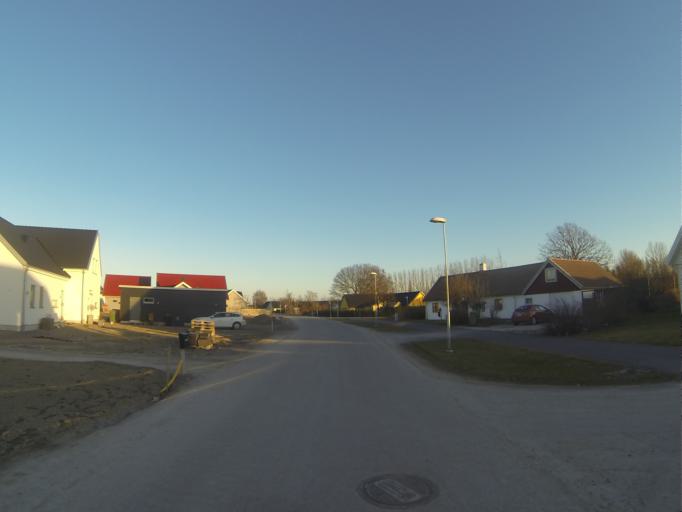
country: SE
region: Skane
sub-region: Staffanstorps Kommun
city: Staffanstorp
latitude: 55.6299
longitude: 13.2009
